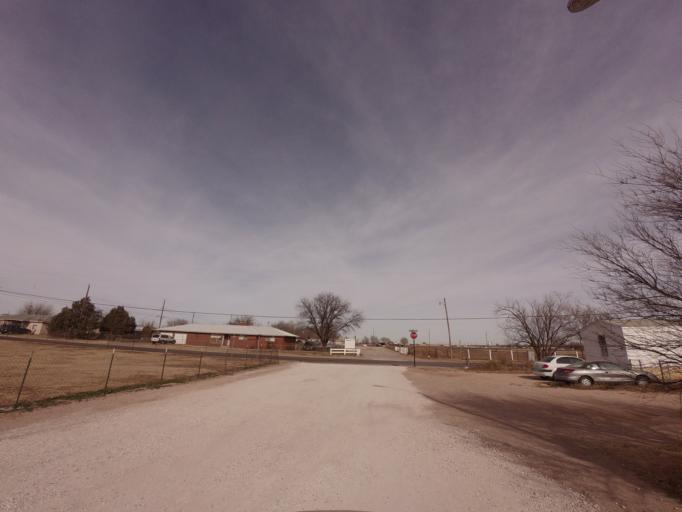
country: US
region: New Mexico
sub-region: Curry County
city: Clovis
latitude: 34.4096
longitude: -103.2342
